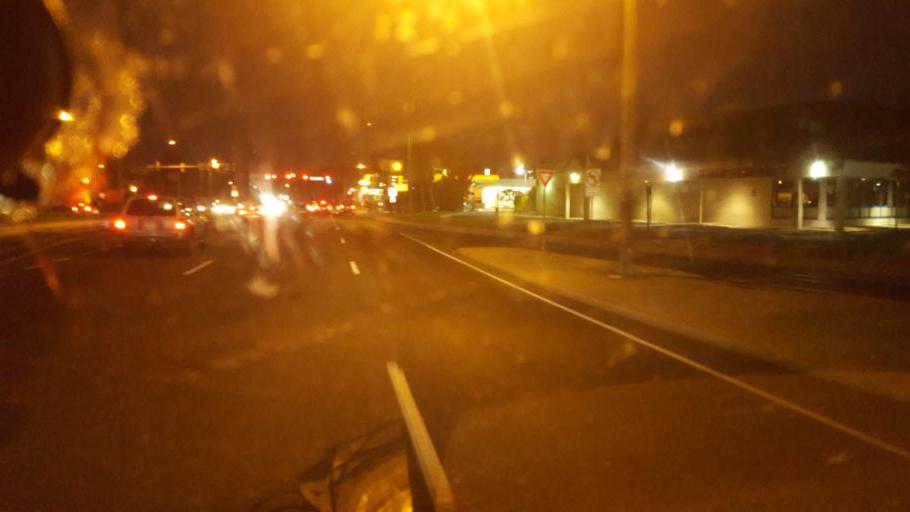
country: US
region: Virginia
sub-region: Fairfax County
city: Lincolnia
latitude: 38.8179
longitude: -77.1420
